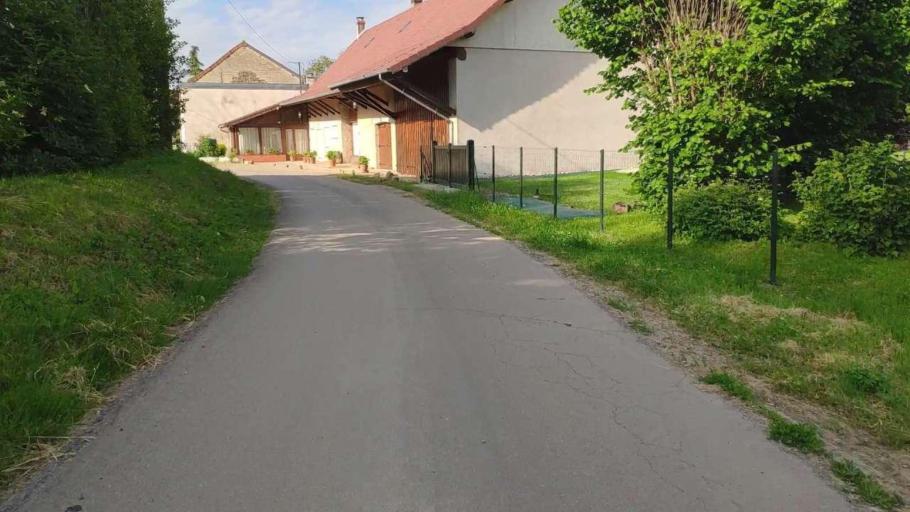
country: FR
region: Franche-Comte
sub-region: Departement du Jura
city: Bletterans
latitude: 46.7382
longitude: 5.4689
